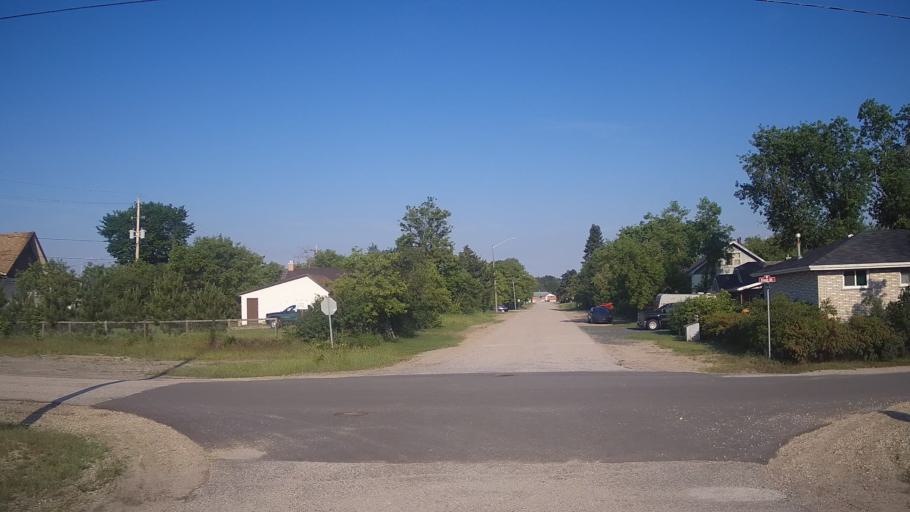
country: CA
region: Ontario
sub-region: Rainy River District
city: Atikokan
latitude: 49.4173
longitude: -91.6587
